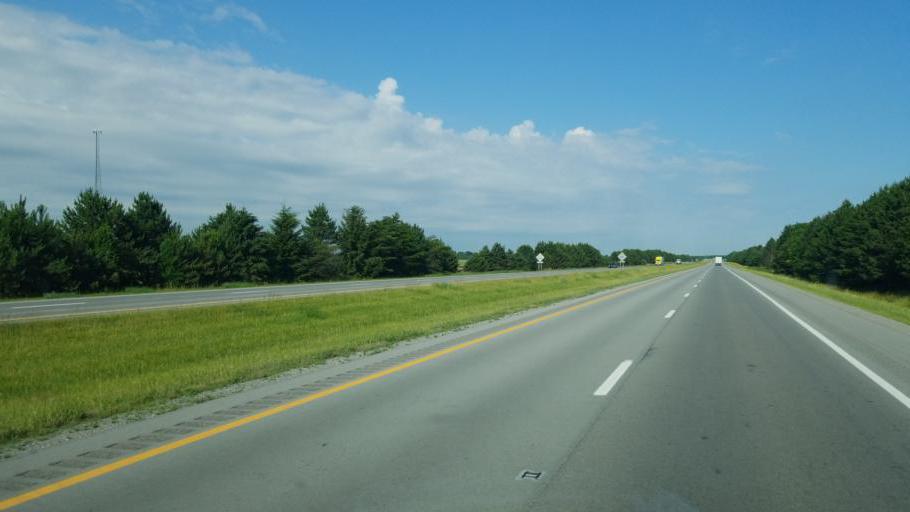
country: US
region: Ohio
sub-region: Hancock County
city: Findlay
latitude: 40.9863
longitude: -83.6149
